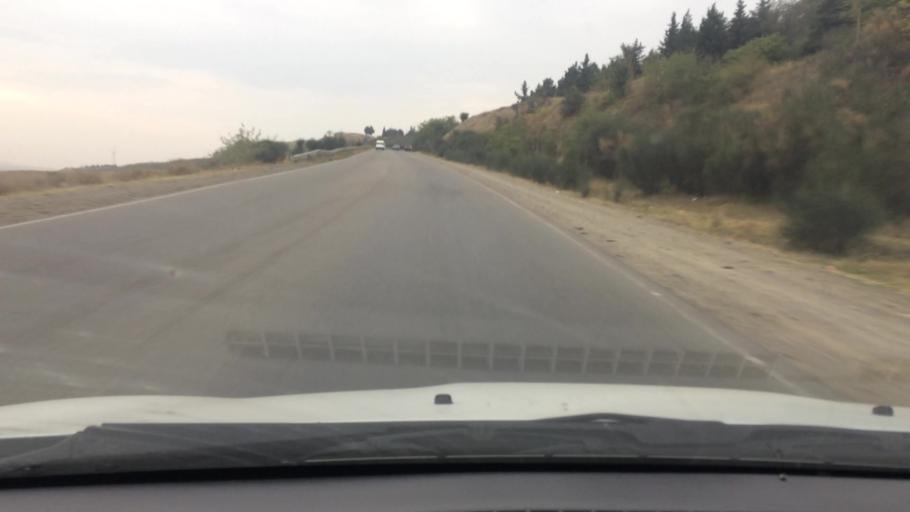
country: GE
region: T'bilisi
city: Tbilisi
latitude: 41.5988
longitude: 44.7786
